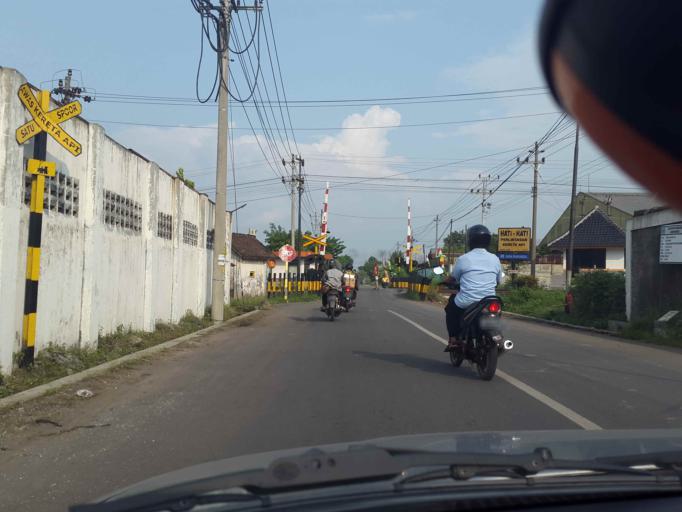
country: ID
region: Central Java
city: Jaten
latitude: -7.5641
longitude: 110.8814
